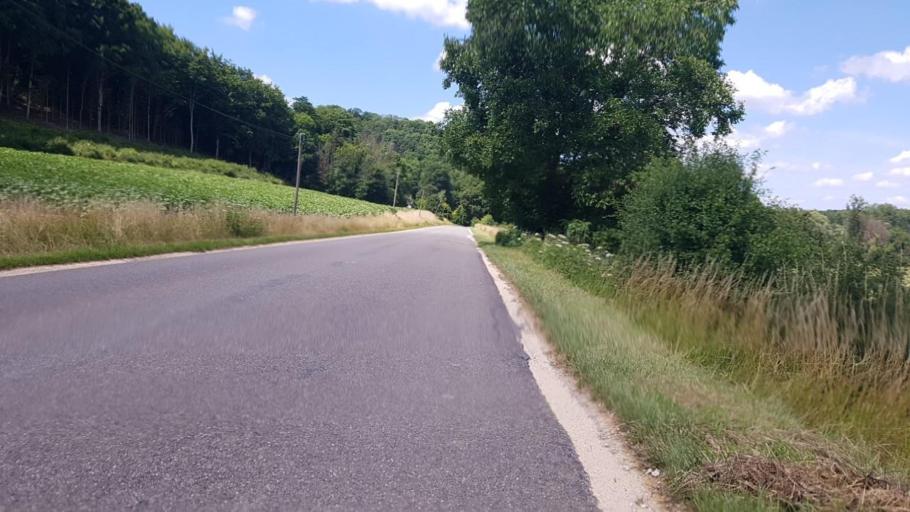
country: FR
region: Lorraine
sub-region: Departement de la Meuse
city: Gondrecourt-le-Chateau
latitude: 48.6322
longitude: 5.4574
